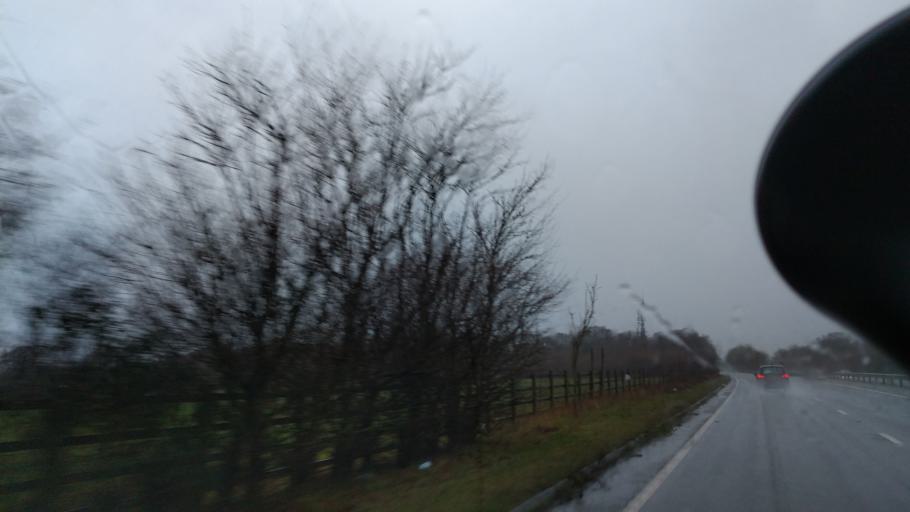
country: GB
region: England
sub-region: West Sussex
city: Rustington
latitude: 50.8402
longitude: -0.4738
